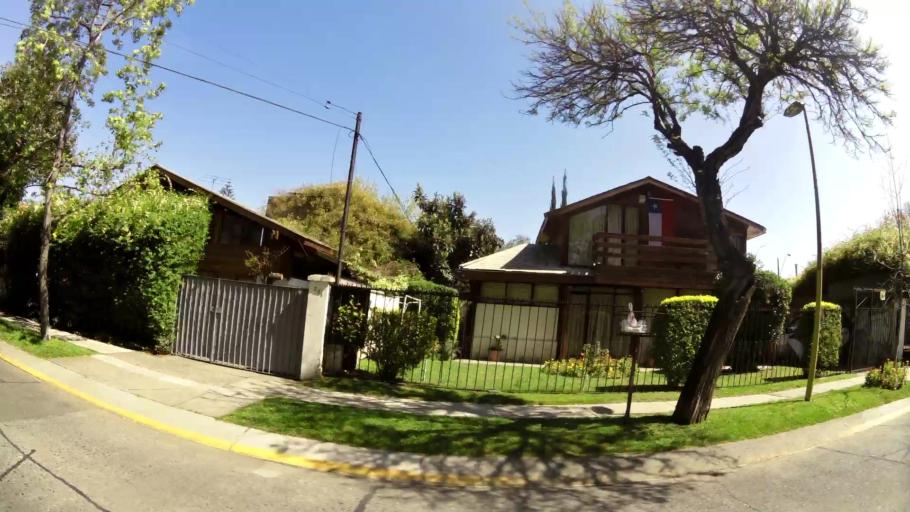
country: CL
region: Santiago Metropolitan
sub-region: Provincia de Santiago
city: Villa Presidente Frei, Nunoa, Santiago, Chile
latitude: -33.4107
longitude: -70.5437
